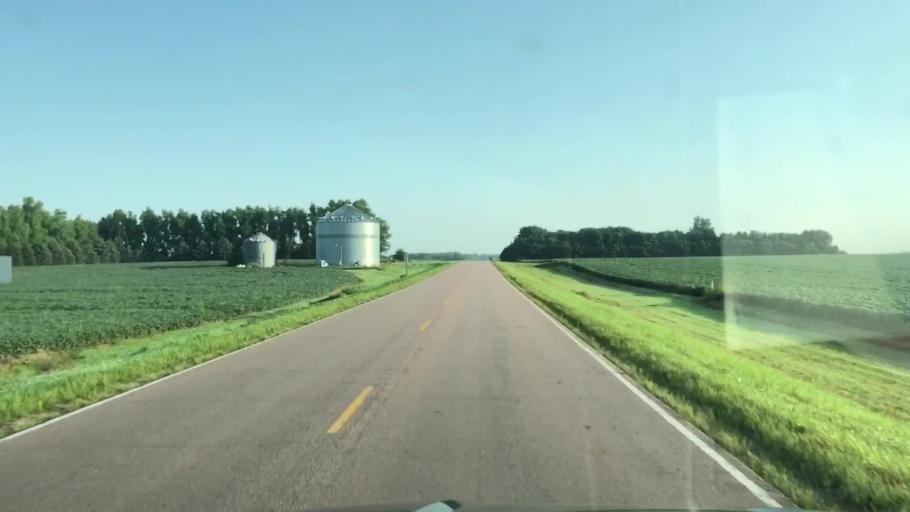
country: US
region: Iowa
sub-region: Lyon County
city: George
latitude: 43.3172
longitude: -95.9990
